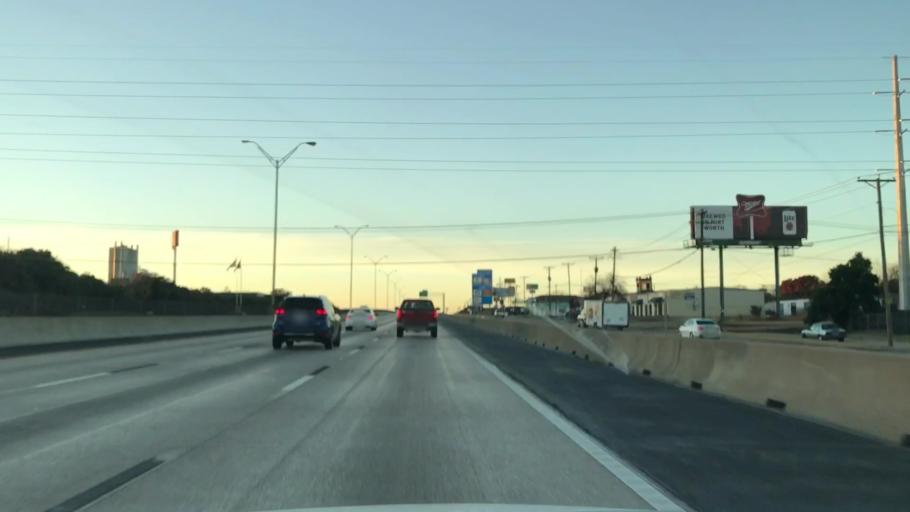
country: US
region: Texas
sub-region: Tarrant County
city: Edgecliff Village
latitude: 32.6463
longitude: -97.3215
